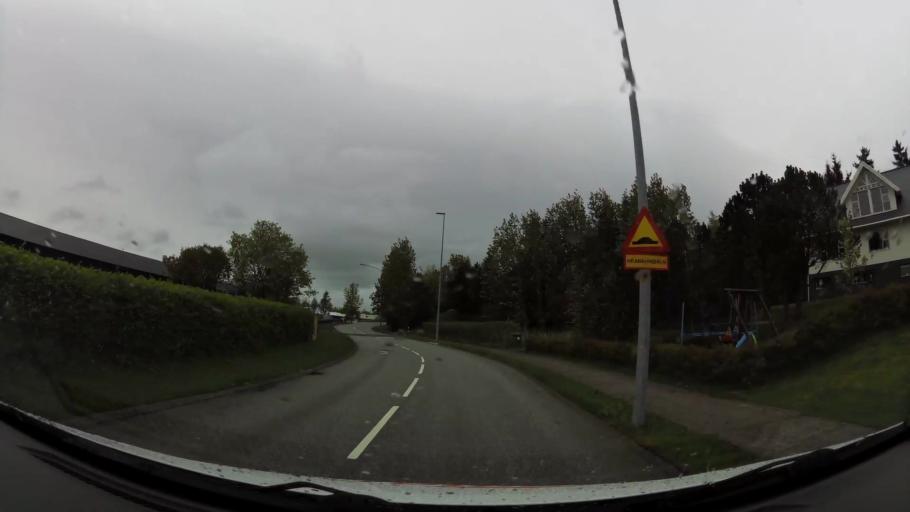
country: IS
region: Capital Region
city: Hafnarfjoerdur
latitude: 64.0697
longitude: -21.9363
